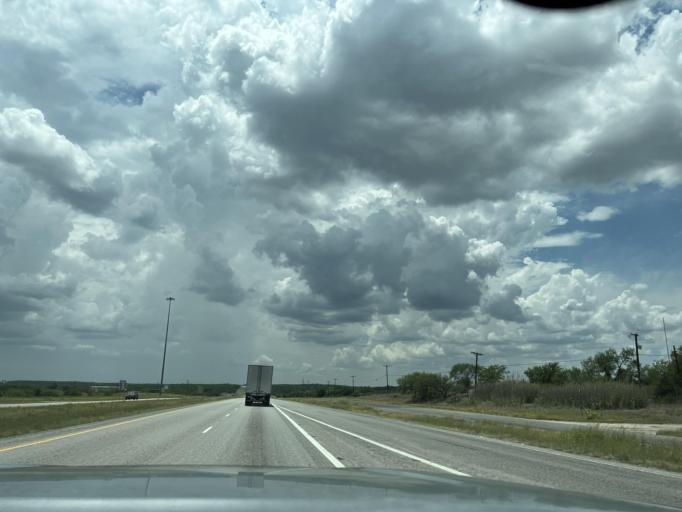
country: US
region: Texas
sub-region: Eastland County
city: Ranger
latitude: 32.4384
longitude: -98.6996
